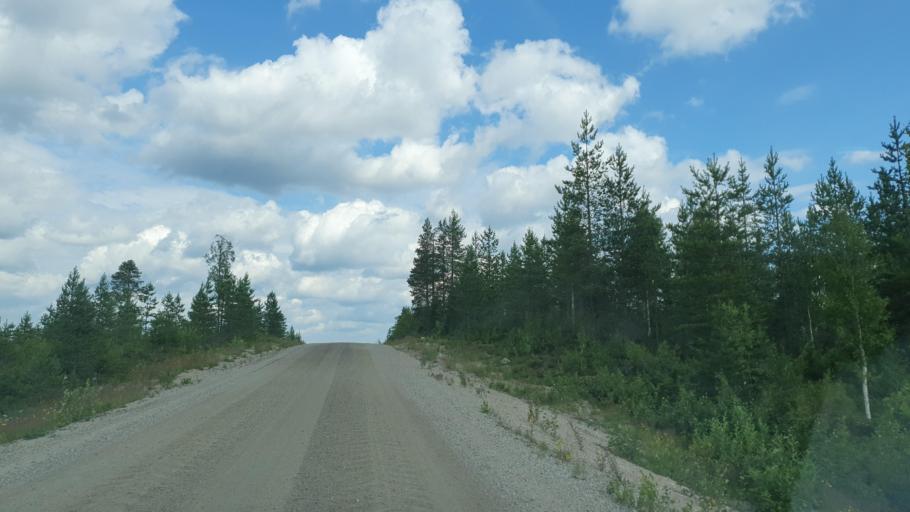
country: FI
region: Kainuu
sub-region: Kehys-Kainuu
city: Kuhmo
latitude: 64.4631
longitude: 29.6008
